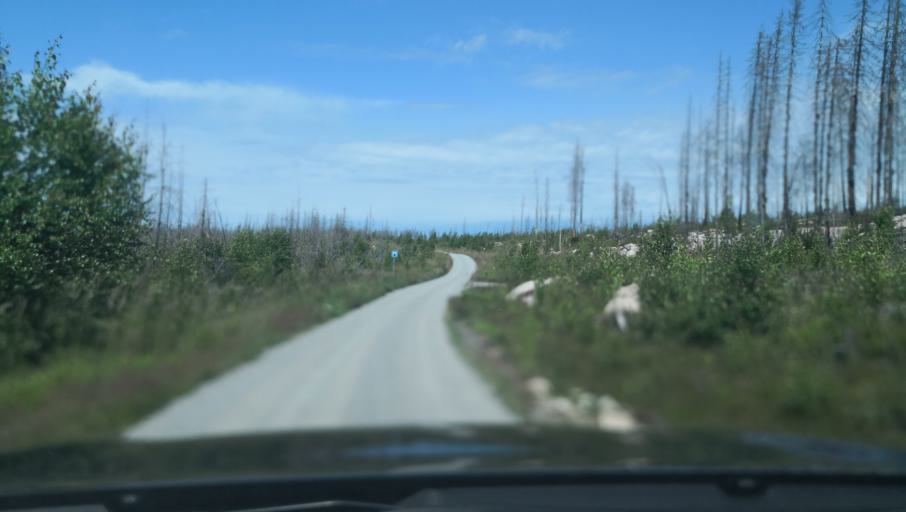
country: SE
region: Vaestmanland
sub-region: Surahammars Kommun
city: Ramnas
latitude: 59.9036
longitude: 16.1450
